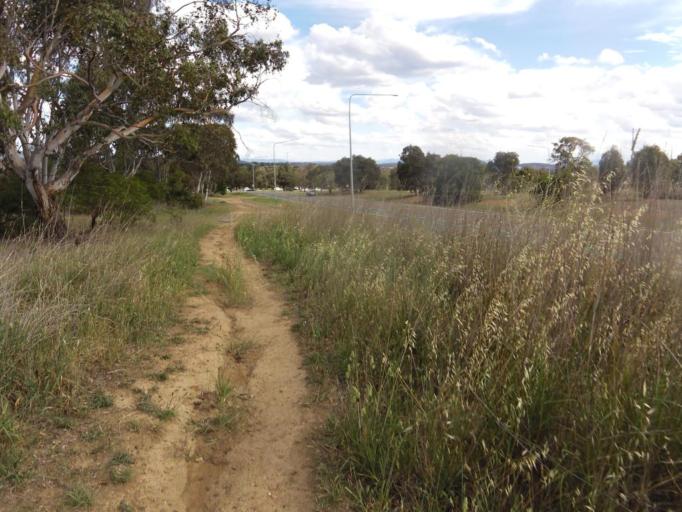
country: AU
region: Australian Capital Territory
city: Belconnen
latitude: -35.1874
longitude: 149.0787
